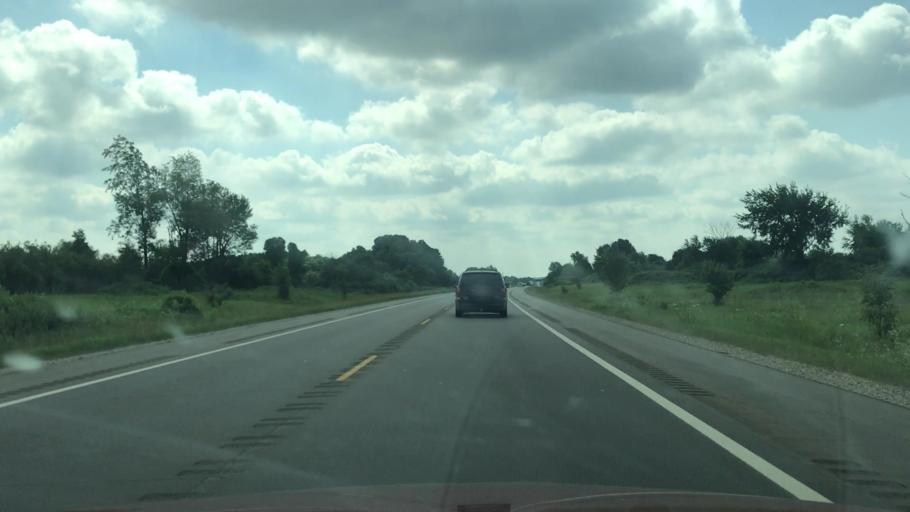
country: US
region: Michigan
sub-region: Kent County
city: Kent City
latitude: 43.2254
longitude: -85.7764
